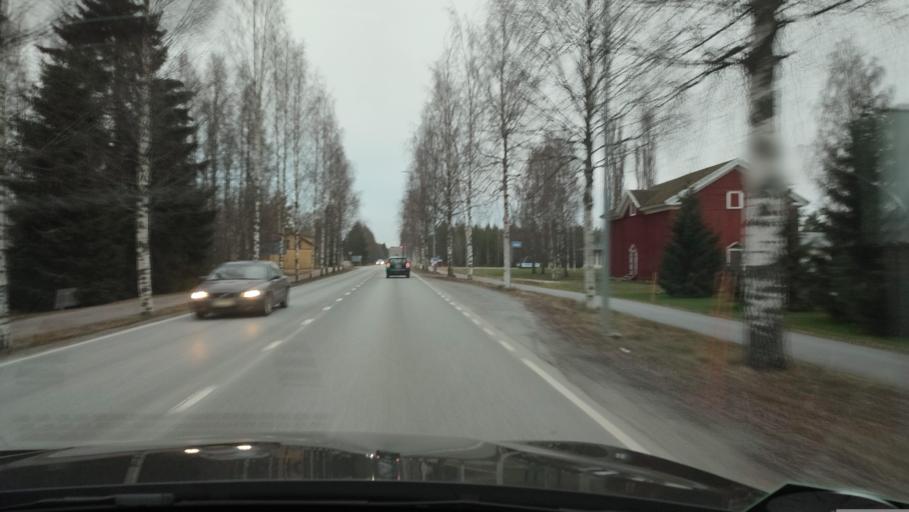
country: FI
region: Southern Ostrobothnia
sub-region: Suupohja
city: Kauhajoki
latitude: 62.4160
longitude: 22.1735
